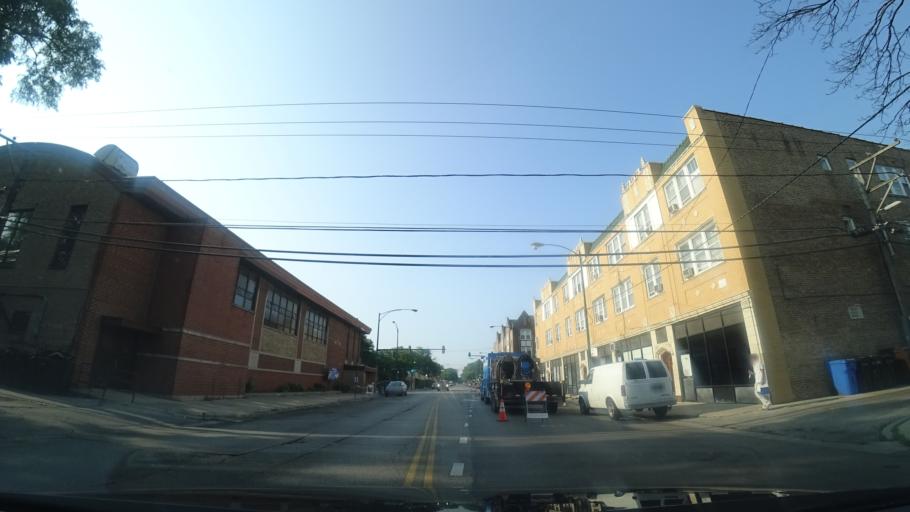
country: US
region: Illinois
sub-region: Cook County
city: Lincolnwood
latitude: 42.0091
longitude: -87.6998
